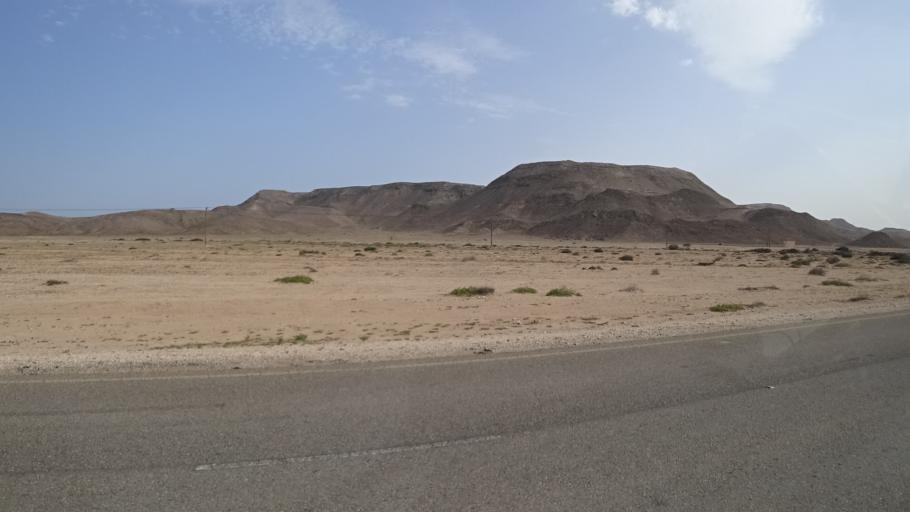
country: OM
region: Ash Sharqiyah
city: Sur
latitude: 22.4352
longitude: 59.8180
